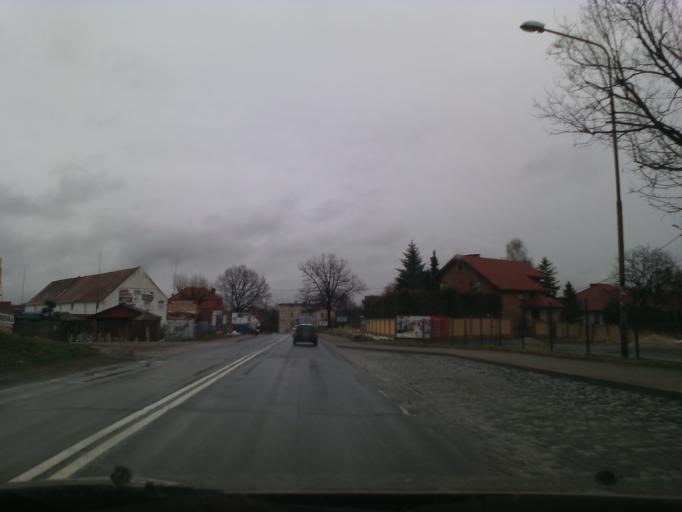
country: PL
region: Lower Silesian Voivodeship
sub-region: Powiat swidnicki
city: Swidnica
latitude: 50.8397
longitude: 16.4425
